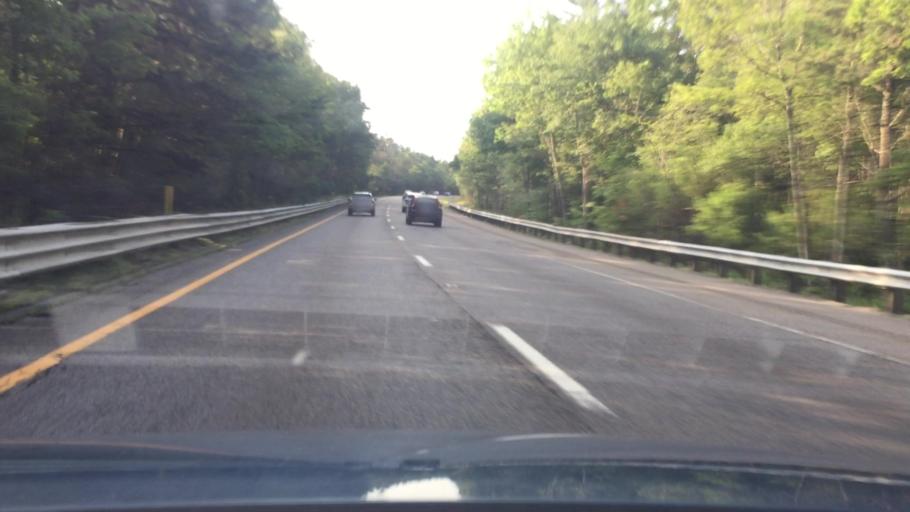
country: US
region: Massachusetts
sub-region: Plymouth County
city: North Pembroke
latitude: 42.1000
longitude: -70.7552
